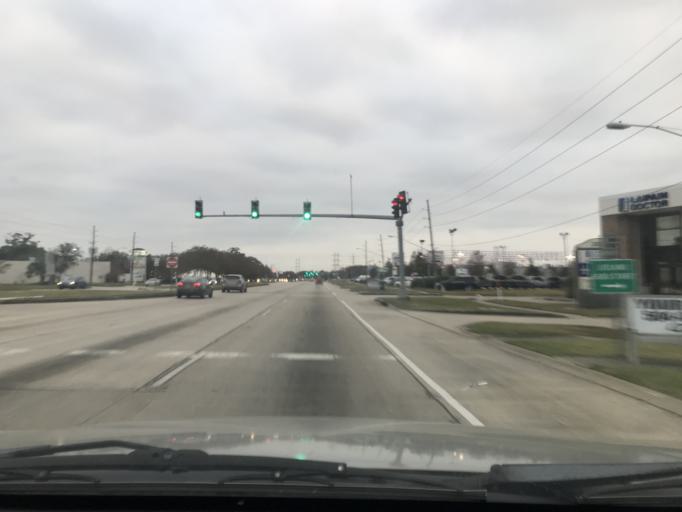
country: US
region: Louisiana
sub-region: Jefferson Parish
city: Woodmere
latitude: 29.8739
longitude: -90.0864
